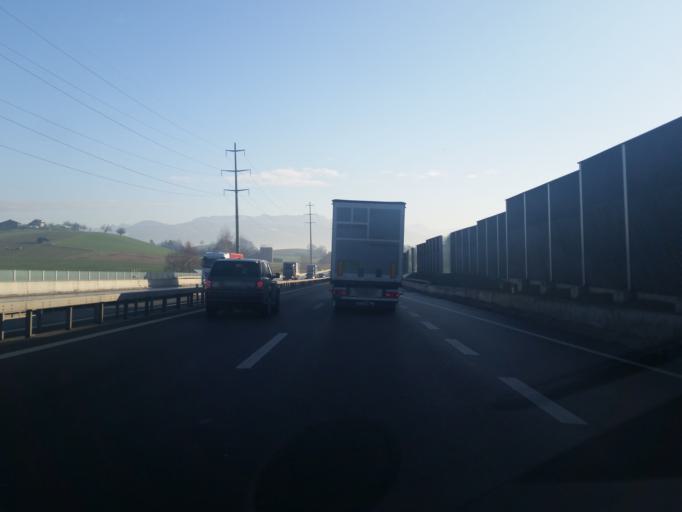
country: CH
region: Zurich
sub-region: Bezirk Affoltern
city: Knonau
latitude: 47.2255
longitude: 8.4642
